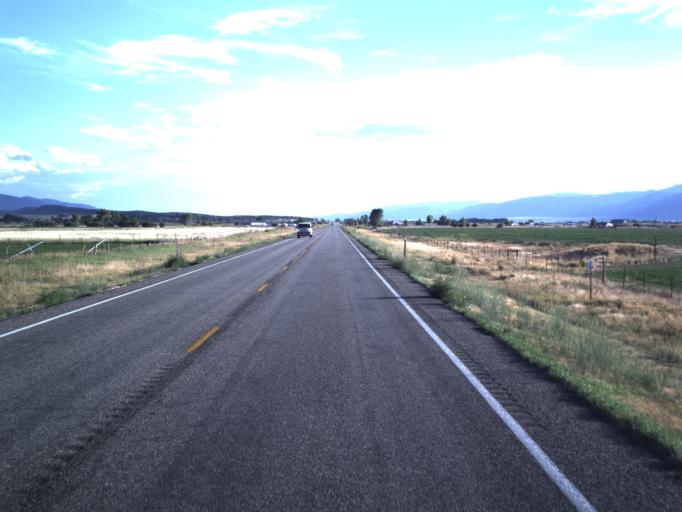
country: US
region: Utah
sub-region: Sanpete County
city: Mount Pleasant
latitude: 39.5096
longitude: -111.4966
